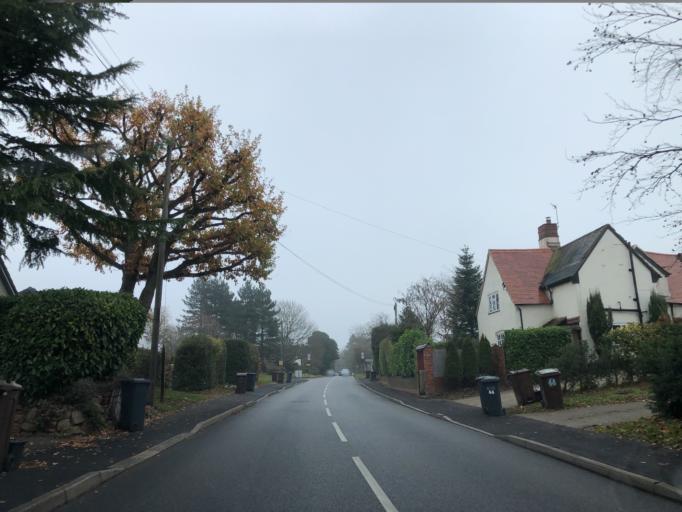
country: GB
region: England
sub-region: Solihull
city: Balsall Common
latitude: 52.3856
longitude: -1.6560
